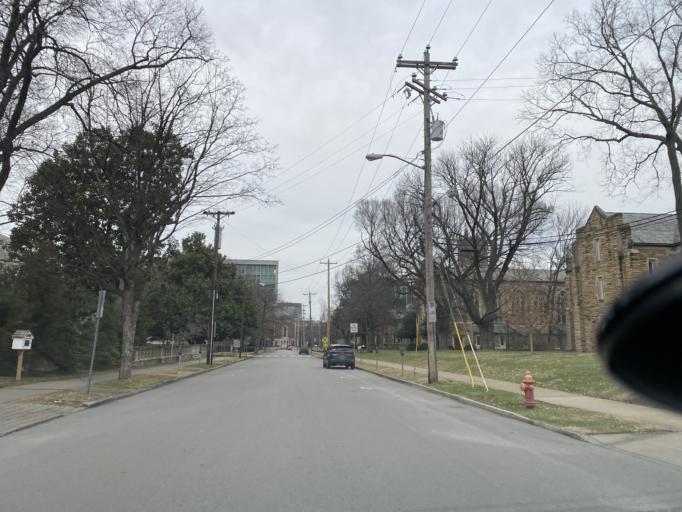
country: US
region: Tennessee
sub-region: Davidson County
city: Nashville
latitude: 36.1451
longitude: -86.7974
